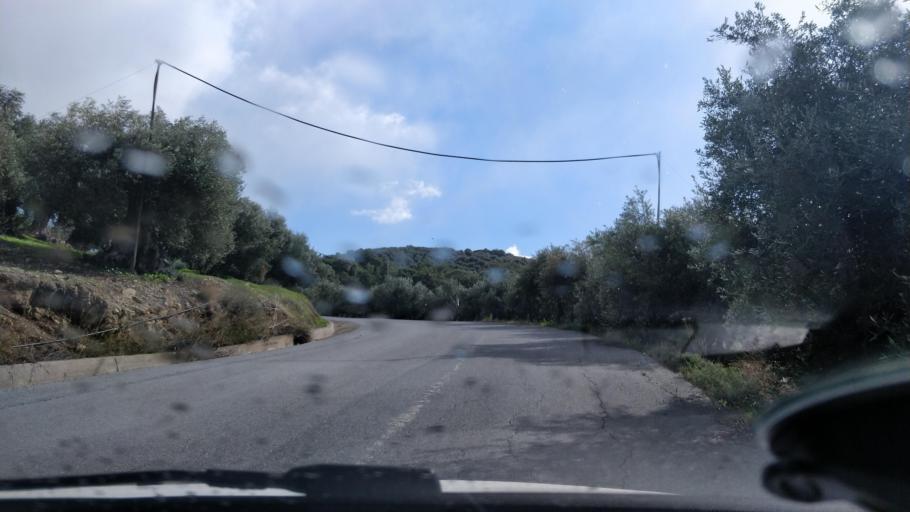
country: GR
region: Crete
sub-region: Nomos Lasithiou
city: Gra Liyia
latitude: 34.9954
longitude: 25.5094
